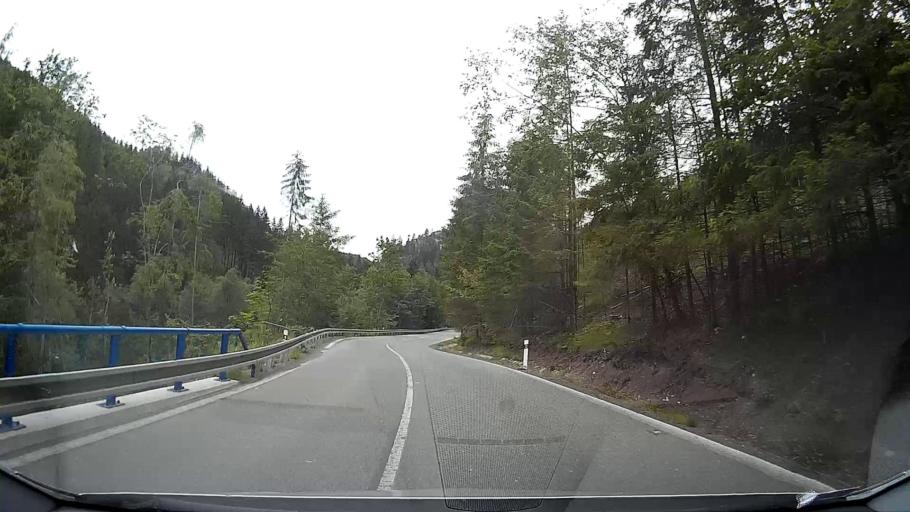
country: SK
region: Presovsky
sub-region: Okres Poprad
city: Poprad
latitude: 48.9384
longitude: 20.2864
